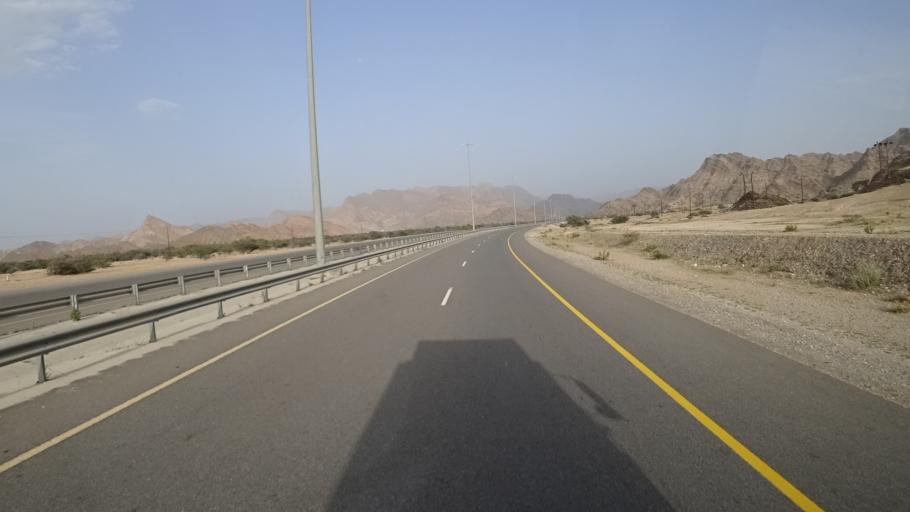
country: OM
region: Muhafazat Masqat
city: Muscat
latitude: 23.3684
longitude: 58.6436
